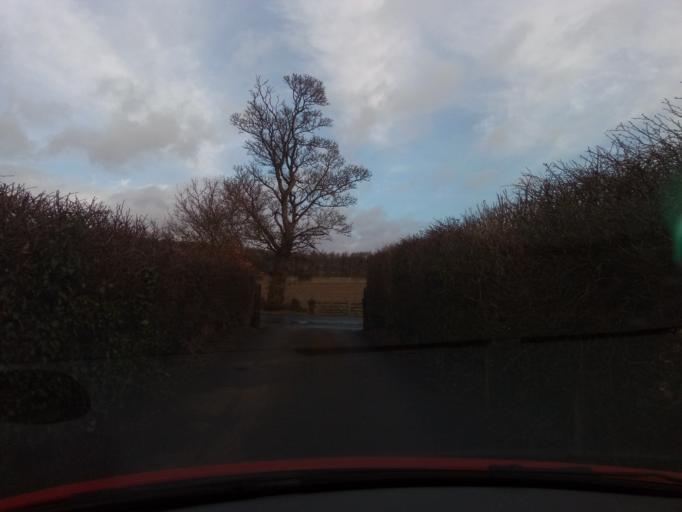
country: GB
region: England
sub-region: Northumberland
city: Corbridge
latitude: 54.9796
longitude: -2.0295
